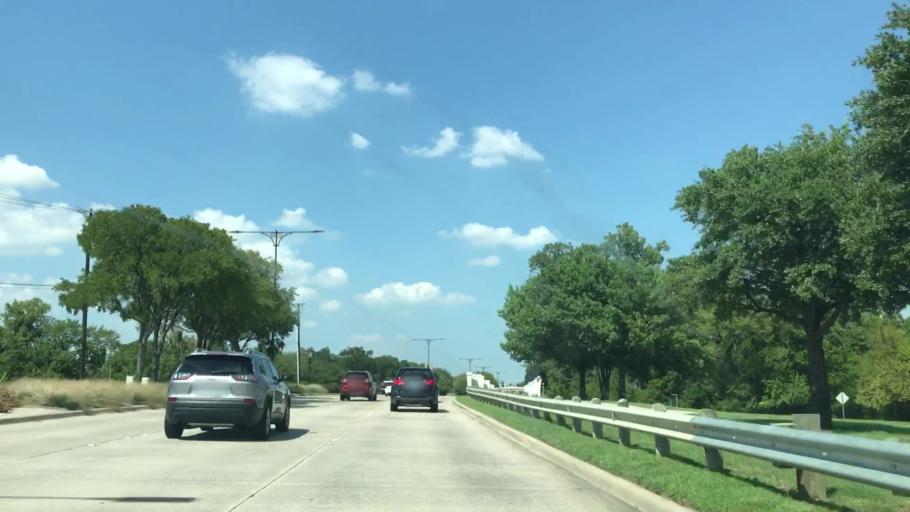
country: US
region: Texas
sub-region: Dallas County
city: Coppell
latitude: 32.9802
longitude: -96.9934
